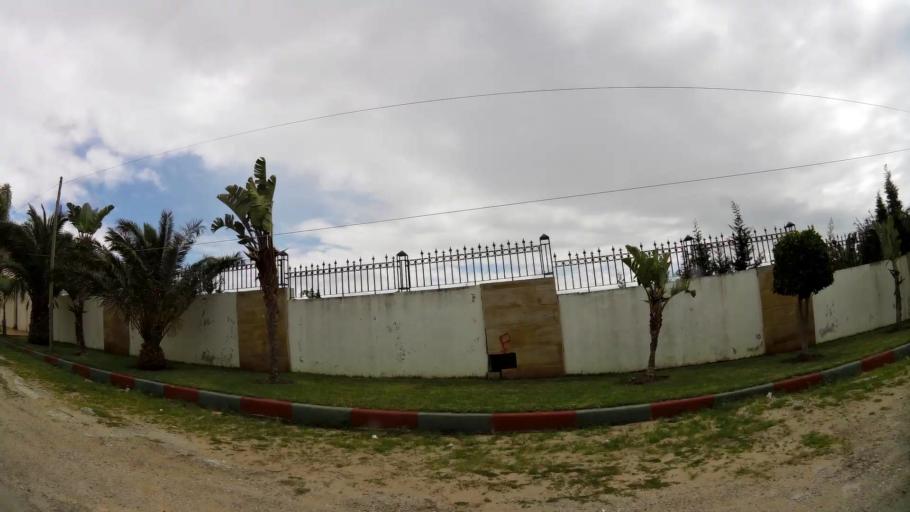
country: MA
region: Tanger-Tetouan
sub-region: Tanger-Assilah
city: Tangier
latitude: 35.7810
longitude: -5.8536
